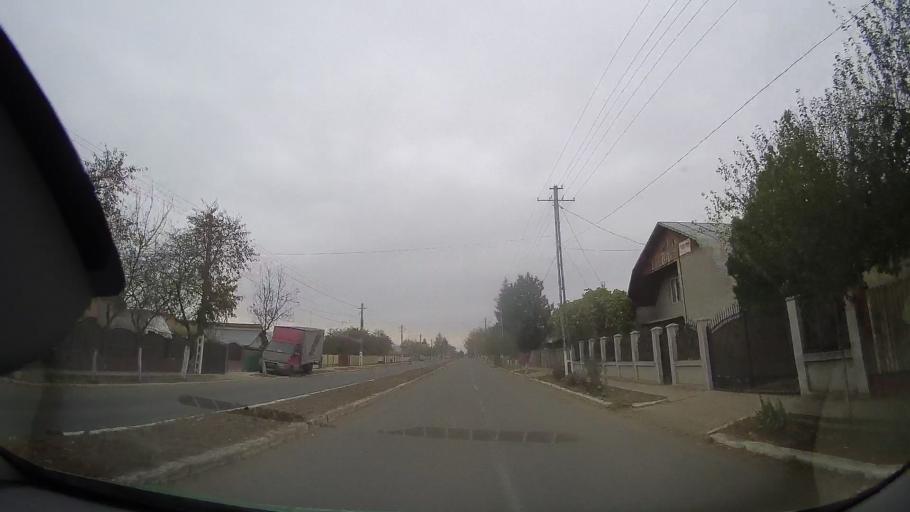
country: RO
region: Buzau
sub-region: Comuna Rusetu
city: Rusetu
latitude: 44.9590
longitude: 27.2155
